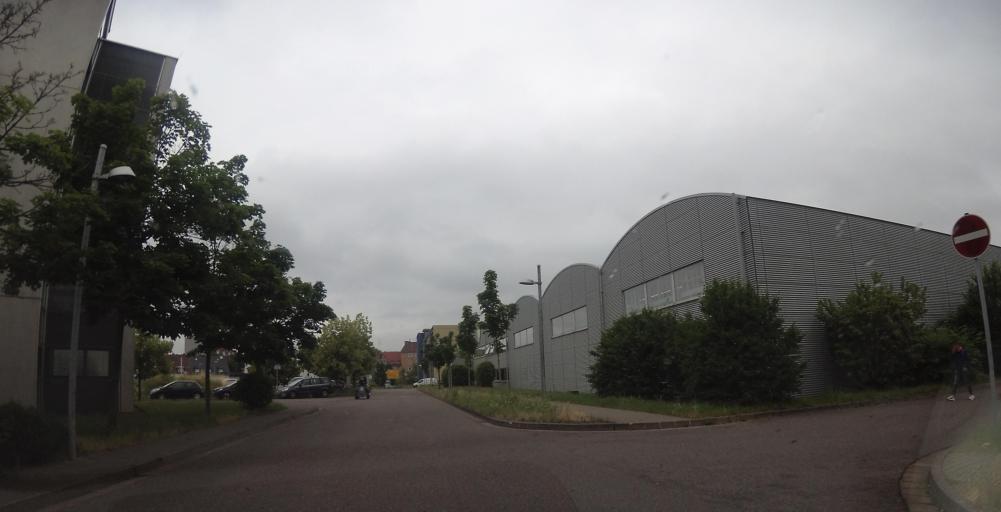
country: DE
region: Saarland
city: Saarbrucken
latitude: 49.2401
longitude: 6.9517
